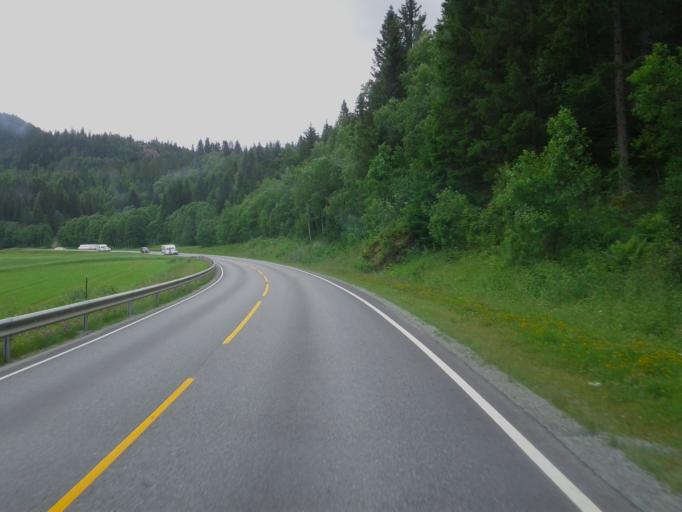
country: NO
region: Sor-Trondelag
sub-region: Midtre Gauldal
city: Storen
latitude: 62.9538
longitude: 10.5914
